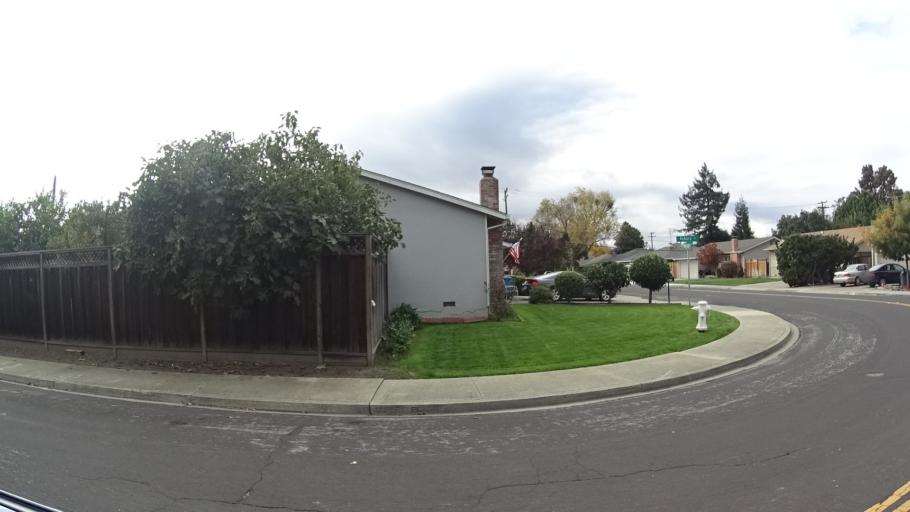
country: US
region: California
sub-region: Santa Clara County
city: Santa Clara
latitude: 37.3389
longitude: -121.9697
